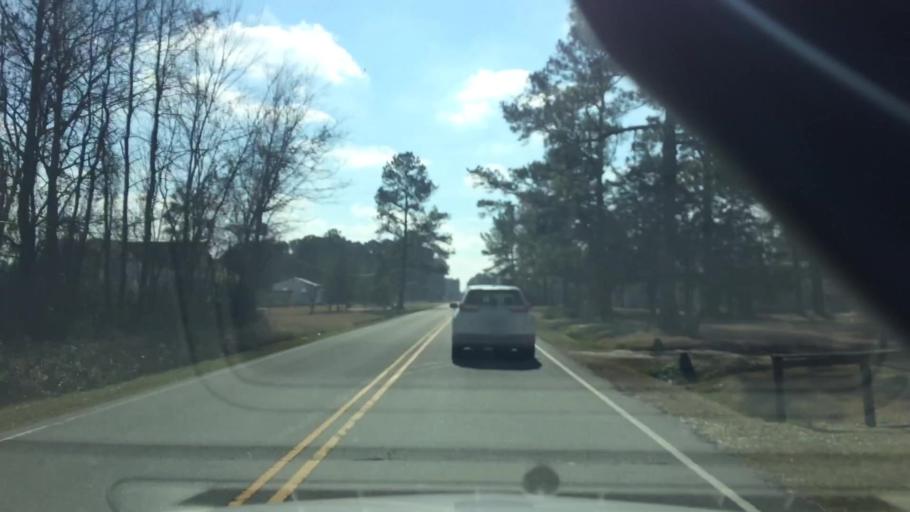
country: US
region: North Carolina
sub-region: Duplin County
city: Beulaville
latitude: 34.8747
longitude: -77.7908
